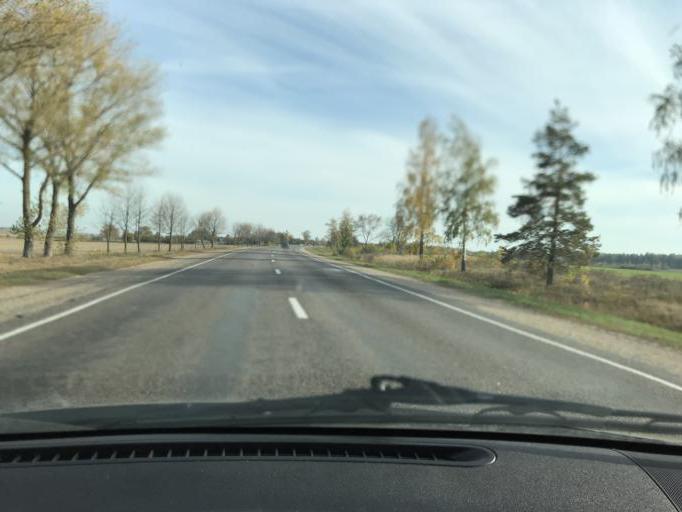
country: BY
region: Brest
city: Lahishyn
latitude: 52.2401
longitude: 26.0023
